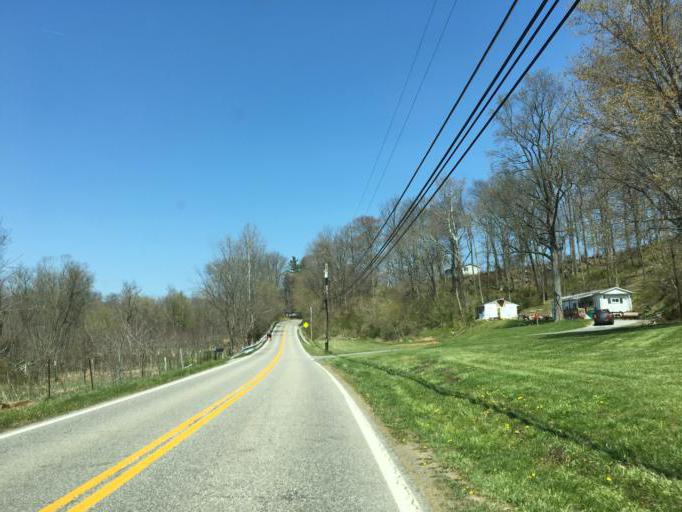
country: US
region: Maryland
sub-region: Frederick County
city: Myersville
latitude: 39.5484
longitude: -77.5256
